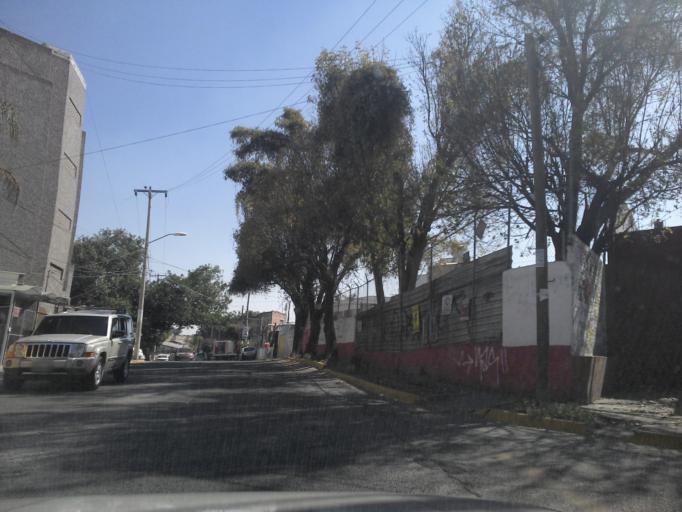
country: MX
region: Jalisco
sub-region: Zapopan
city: Zapopan
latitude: 20.7063
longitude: -103.3597
